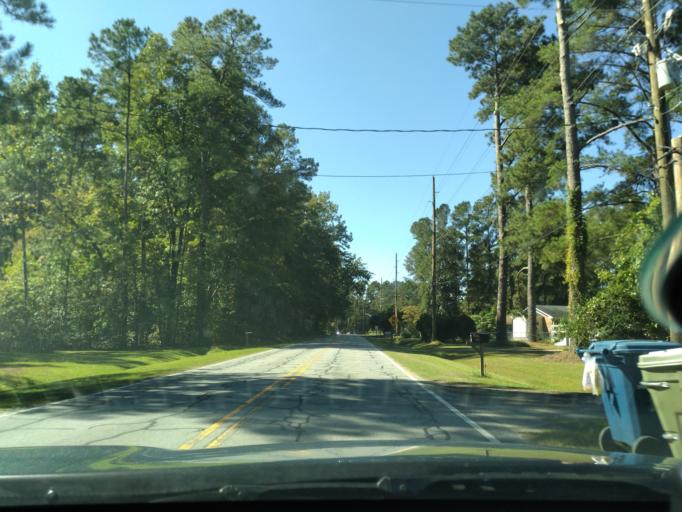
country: US
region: North Carolina
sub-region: Beaufort County
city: Washington
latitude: 35.5550
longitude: -77.0141
